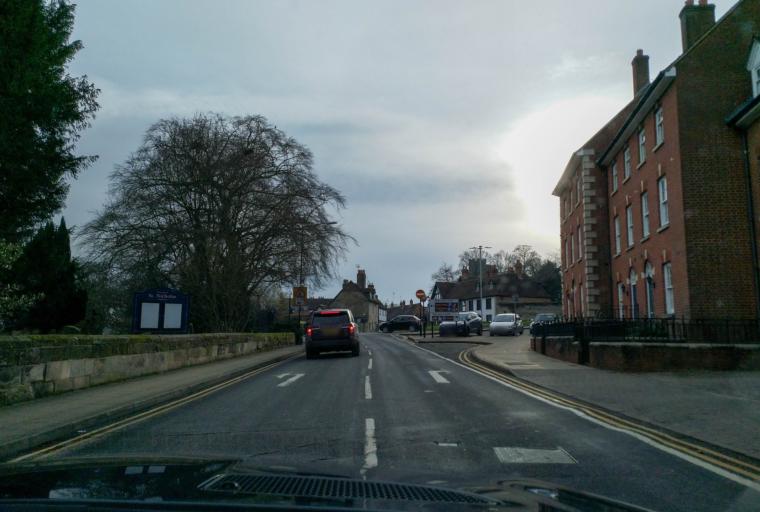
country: GB
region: England
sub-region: Warwickshire
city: Warwick
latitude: 52.2820
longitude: -1.5823
